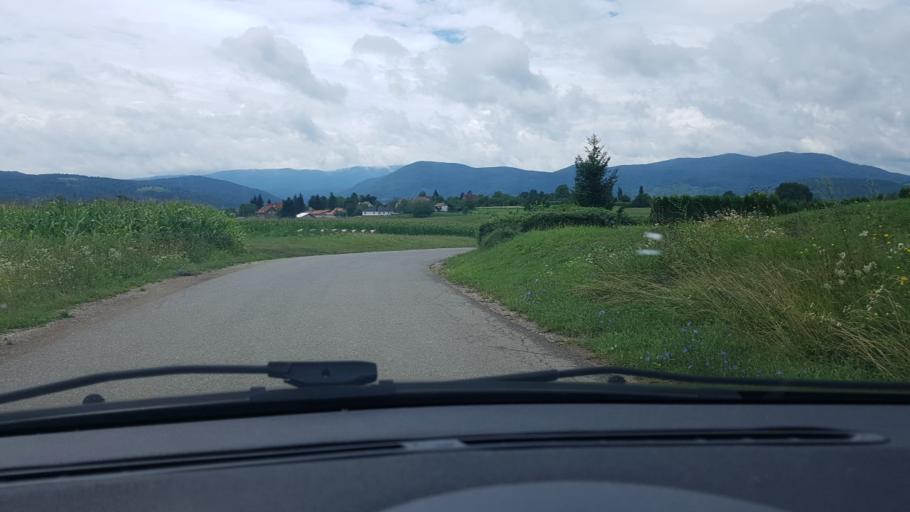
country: HR
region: Licko-Senjska
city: Jezerce
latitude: 44.9562
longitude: 15.6790
